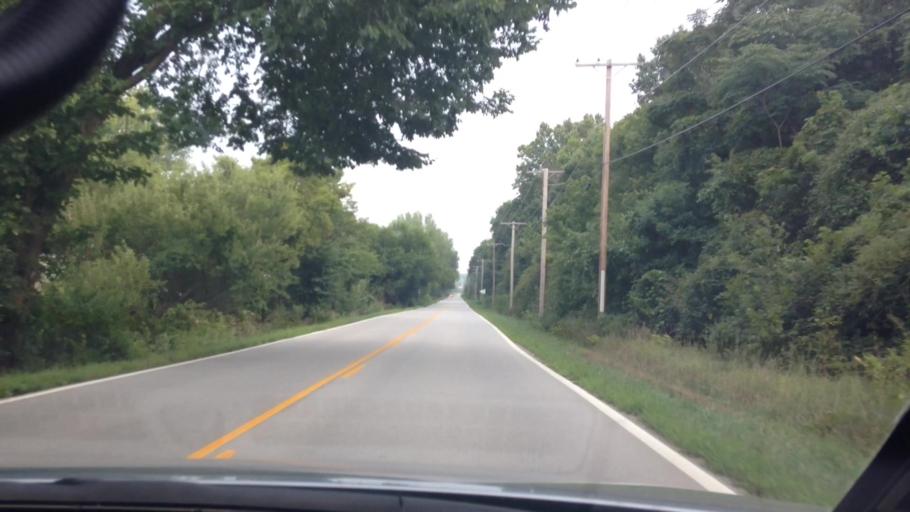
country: US
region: Kansas
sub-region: Leavenworth County
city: Lansing
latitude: 39.1986
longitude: -94.8144
